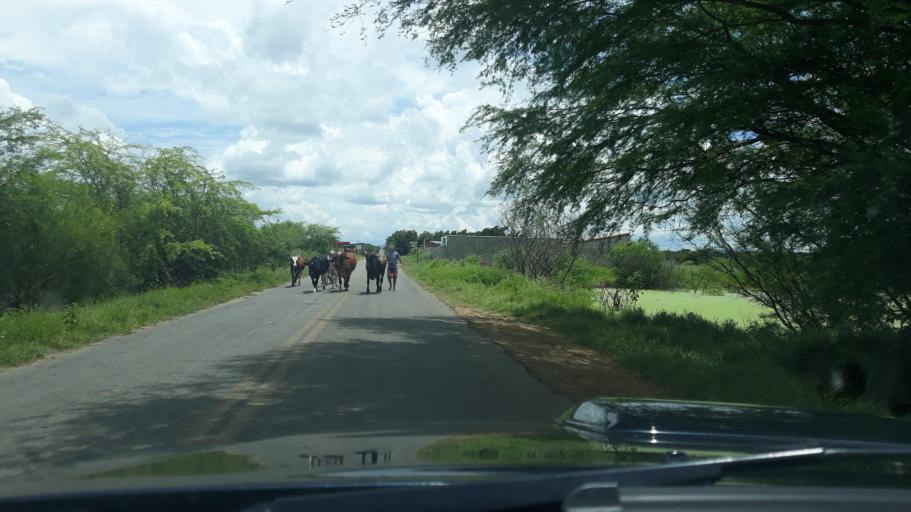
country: BR
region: Bahia
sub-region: Guanambi
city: Guanambi
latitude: -13.9137
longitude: -42.8438
